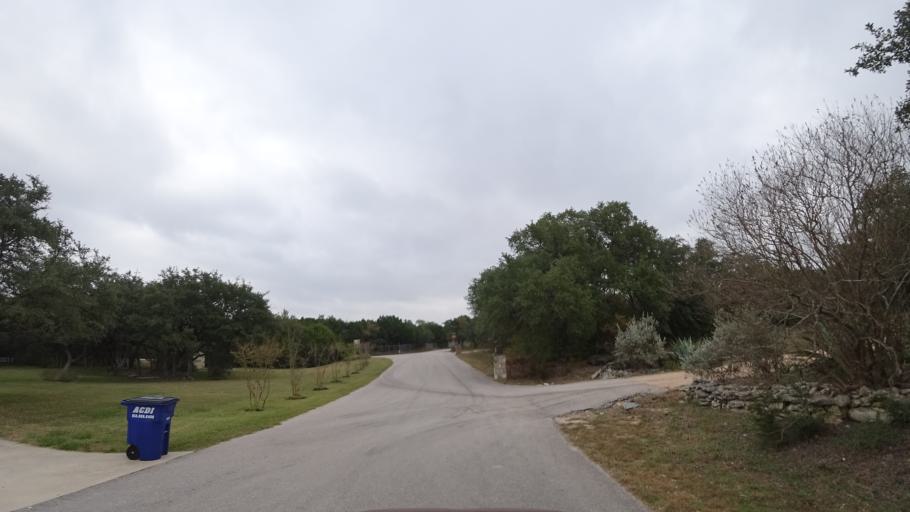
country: US
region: Texas
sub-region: Williamson County
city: Anderson Mill
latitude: 30.4472
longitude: -97.8372
